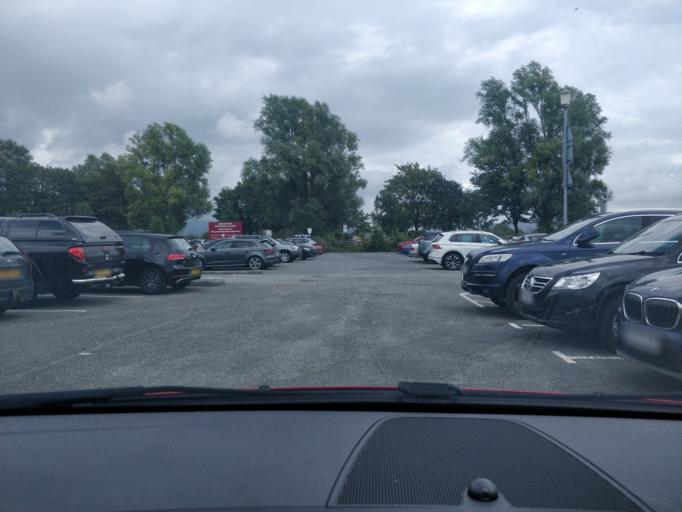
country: GB
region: Wales
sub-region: Gwynedd
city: Porthmadog
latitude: 52.9273
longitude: -4.1284
